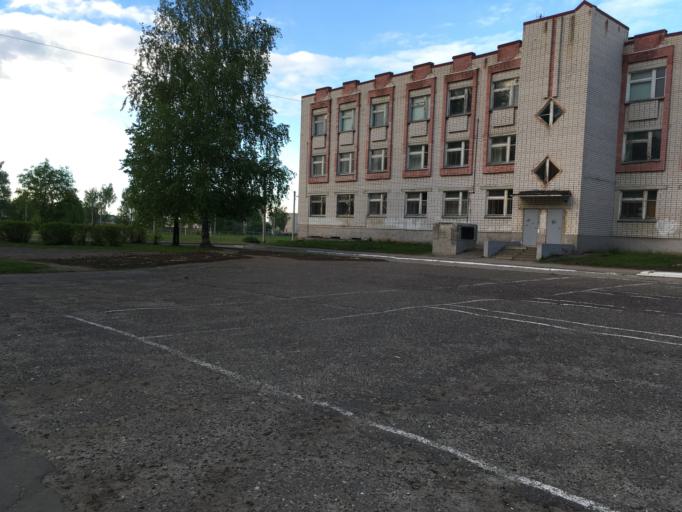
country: RU
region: Mariy-El
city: Yoshkar-Ola
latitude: 56.6522
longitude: 47.8685
